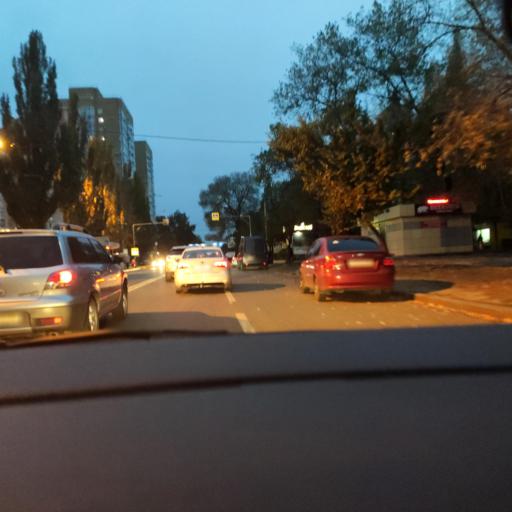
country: RU
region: Voronezj
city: Voronezh
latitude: 51.7015
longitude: 39.1961
